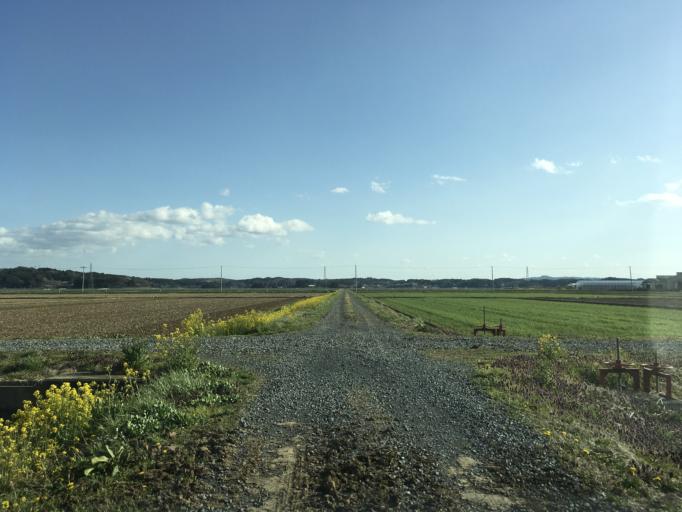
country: JP
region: Miyagi
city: Wakuya
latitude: 38.6626
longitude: 141.2419
